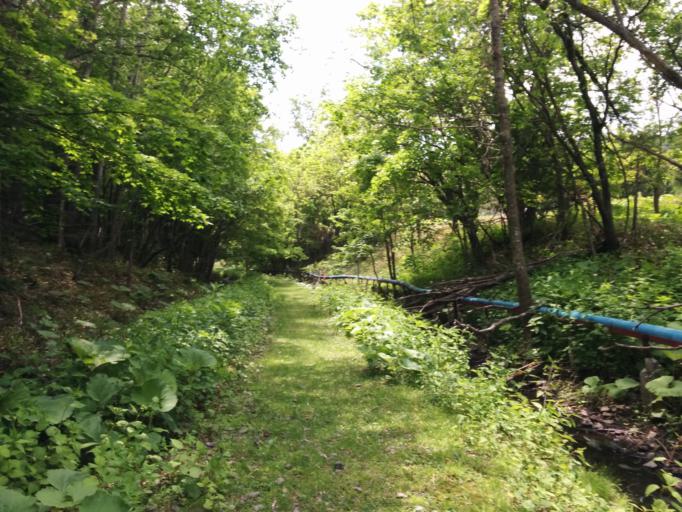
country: JP
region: Hokkaido
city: Otofuke
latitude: 43.3672
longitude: 143.1936
